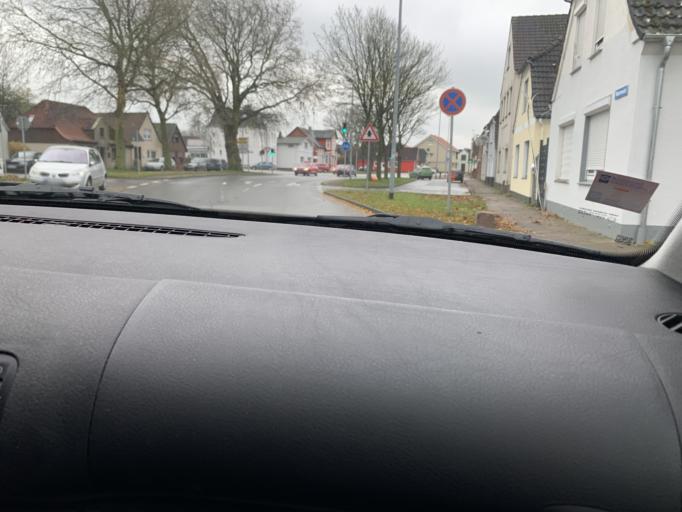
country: DE
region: Schleswig-Holstein
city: Wesseln
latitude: 54.1961
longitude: 9.0870
